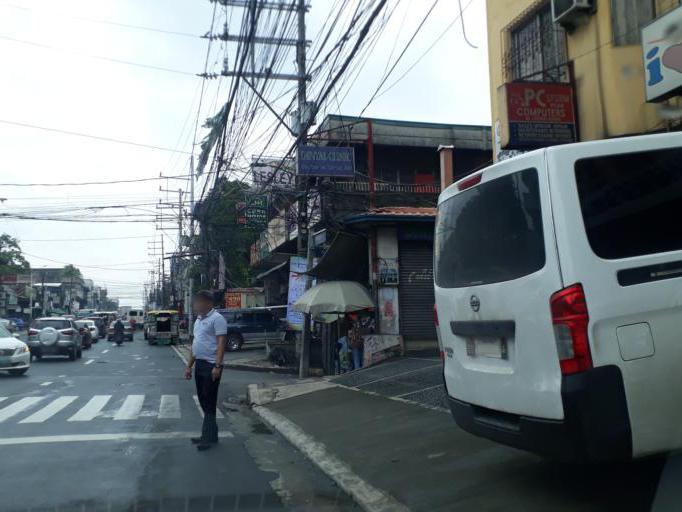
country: PH
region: Calabarzon
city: Del Monte
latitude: 14.6548
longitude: 121.0186
